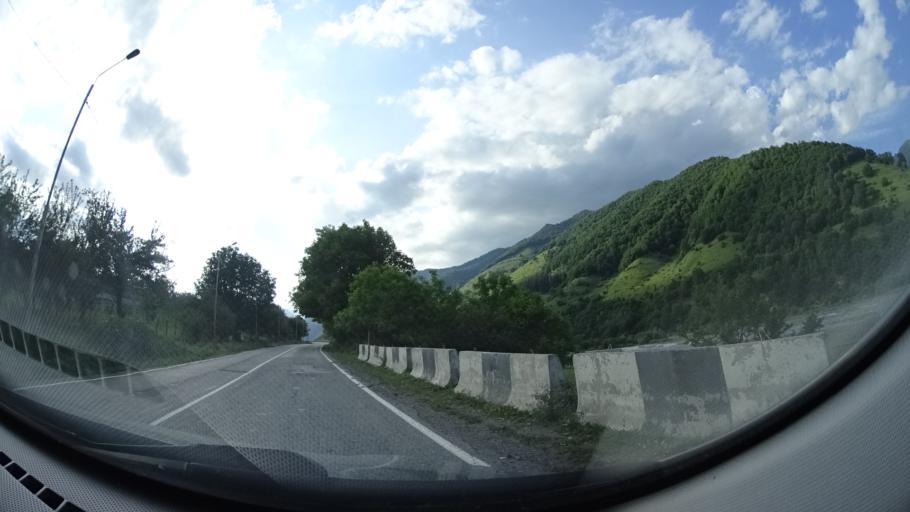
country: GE
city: Gudauri
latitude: 42.4260
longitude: 44.5651
